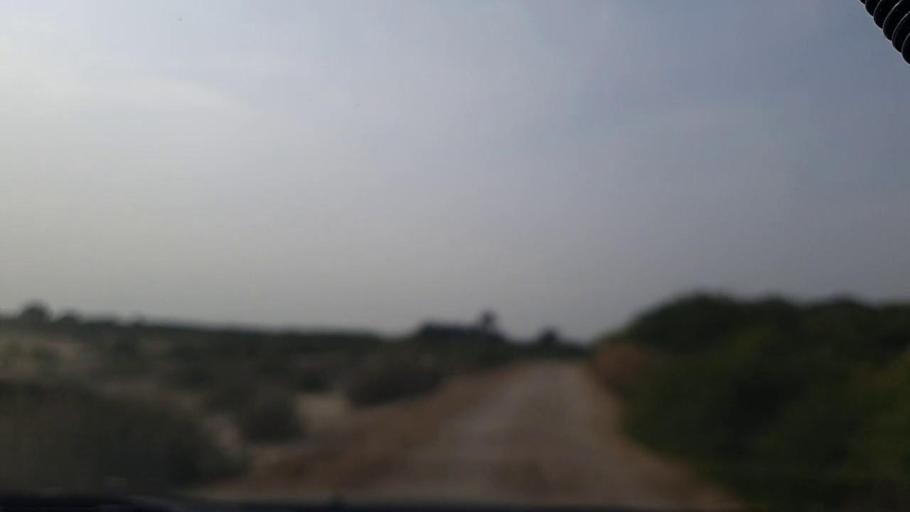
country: PK
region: Sindh
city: Thatta
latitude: 24.6131
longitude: 67.9548
